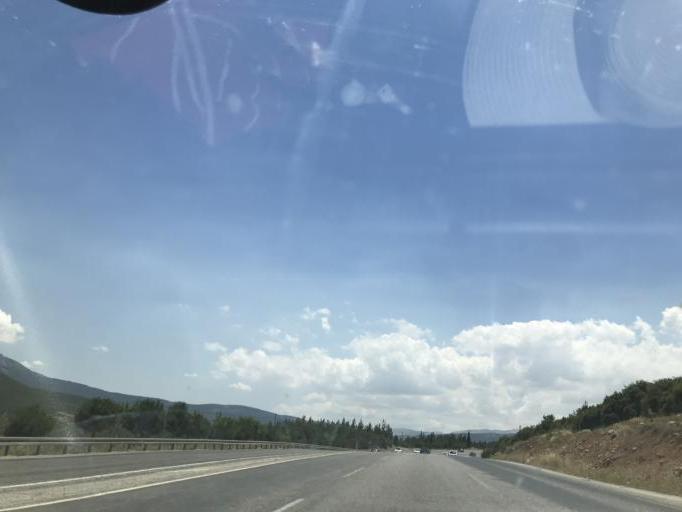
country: TR
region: Denizli
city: Honaz
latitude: 37.7088
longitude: 29.2047
